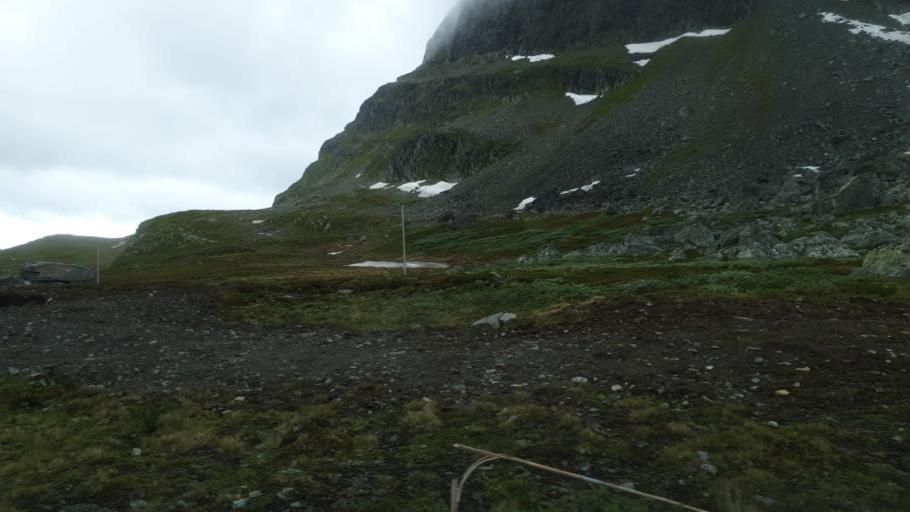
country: NO
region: Oppland
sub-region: Vestre Slidre
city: Slidre
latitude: 61.2998
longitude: 8.8102
